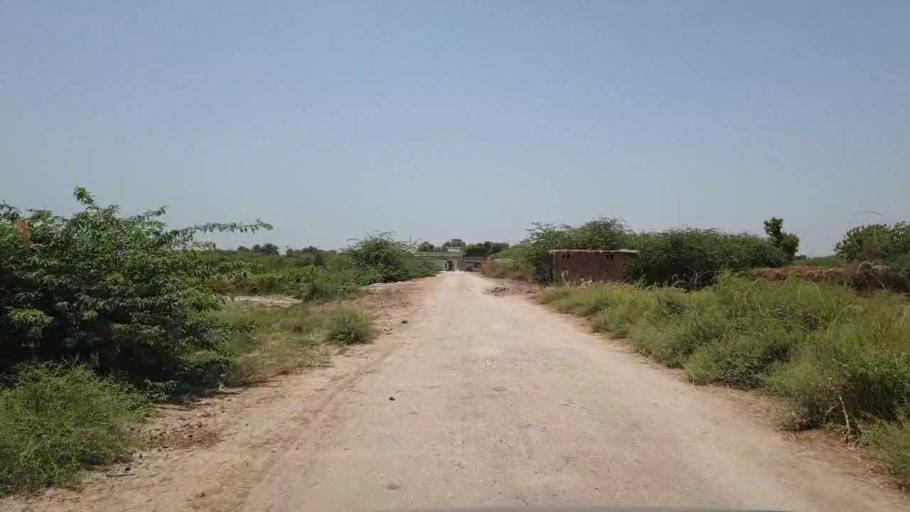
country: PK
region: Sindh
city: Sakrand
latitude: 26.1098
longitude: 68.3896
